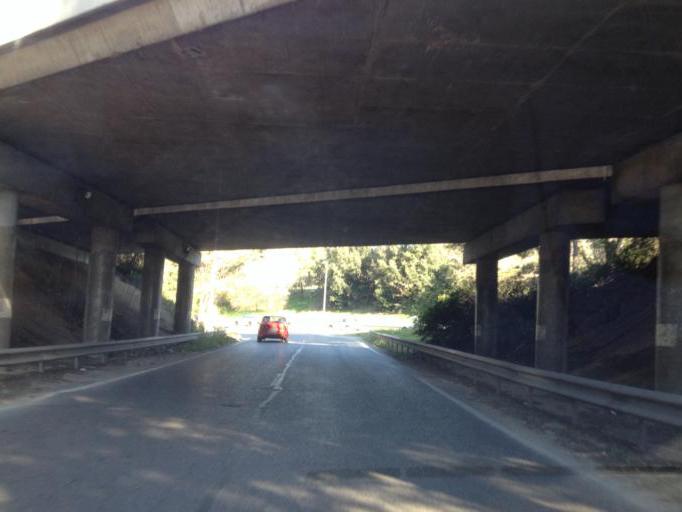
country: FR
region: Provence-Alpes-Cote d'Azur
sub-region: Departement des Bouches-du-Rhone
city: Bouc-Bel-Air
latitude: 43.5030
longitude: 5.3936
